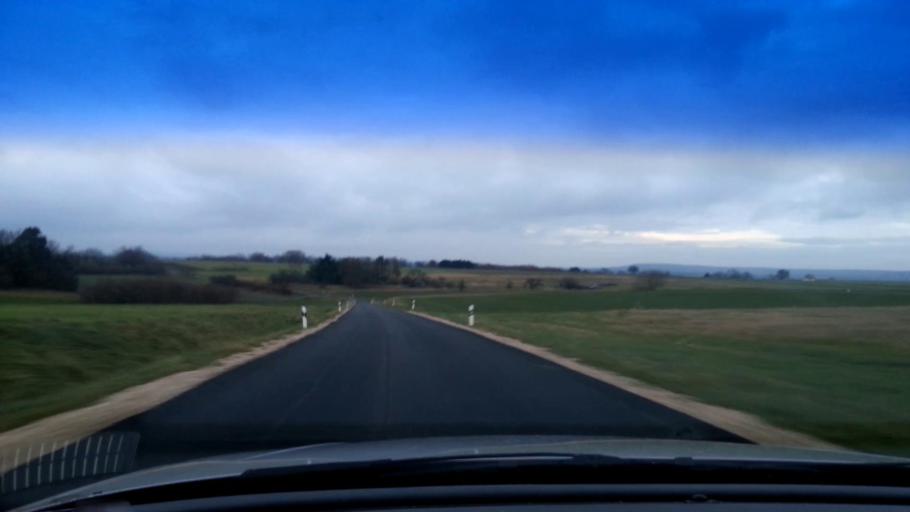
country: DE
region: Bavaria
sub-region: Upper Franconia
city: Viereth-Trunstadt
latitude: 49.9077
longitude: 10.7759
